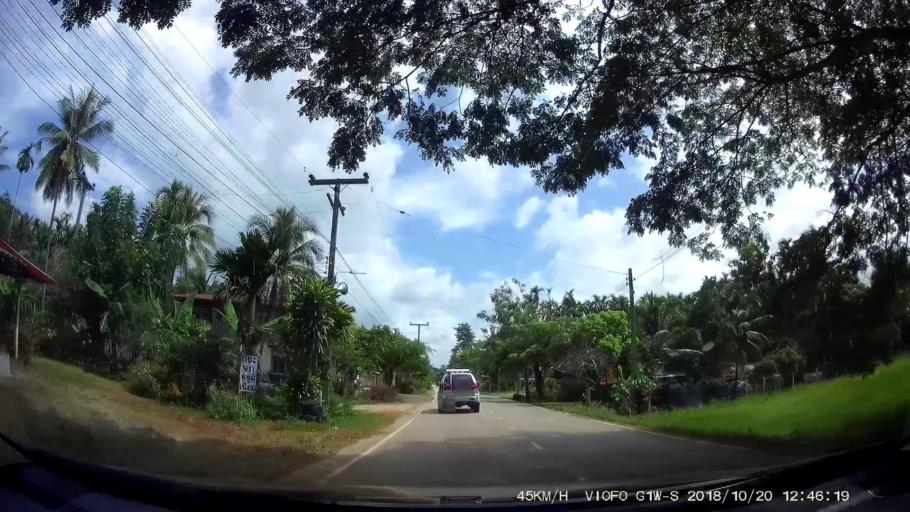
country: TH
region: Chaiyaphum
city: Khon San
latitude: 16.5339
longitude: 101.8795
